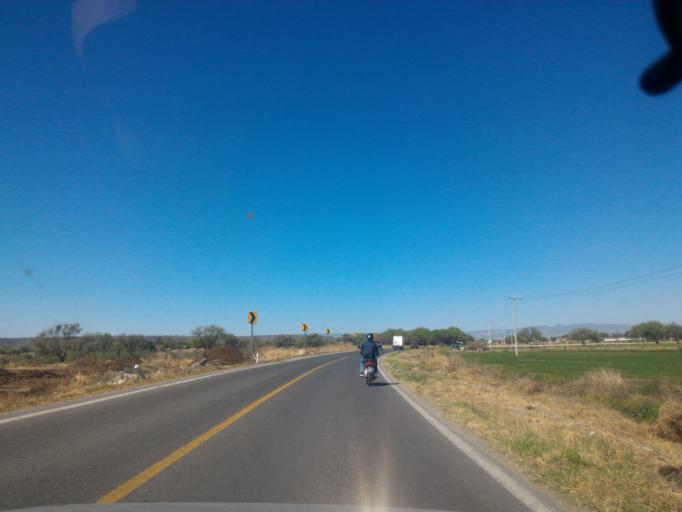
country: MX
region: Guanajuato
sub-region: San Francisco del Rincon
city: San Roque de Montes
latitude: 21.0104
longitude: -101.8018
